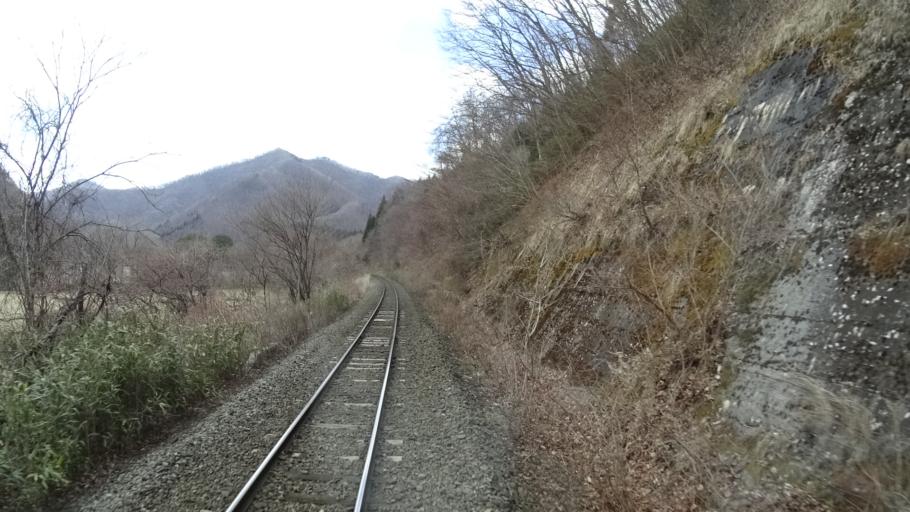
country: JP
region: Iwate
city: Tono
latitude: 39.2558
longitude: 141.6391
